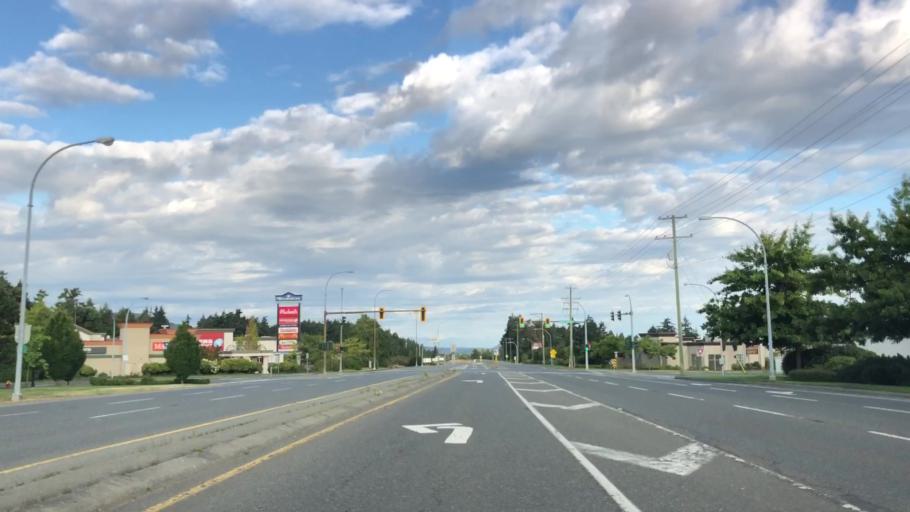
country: CA
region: British Columbia
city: Nanaimo
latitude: 49.2398
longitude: -124.0528
